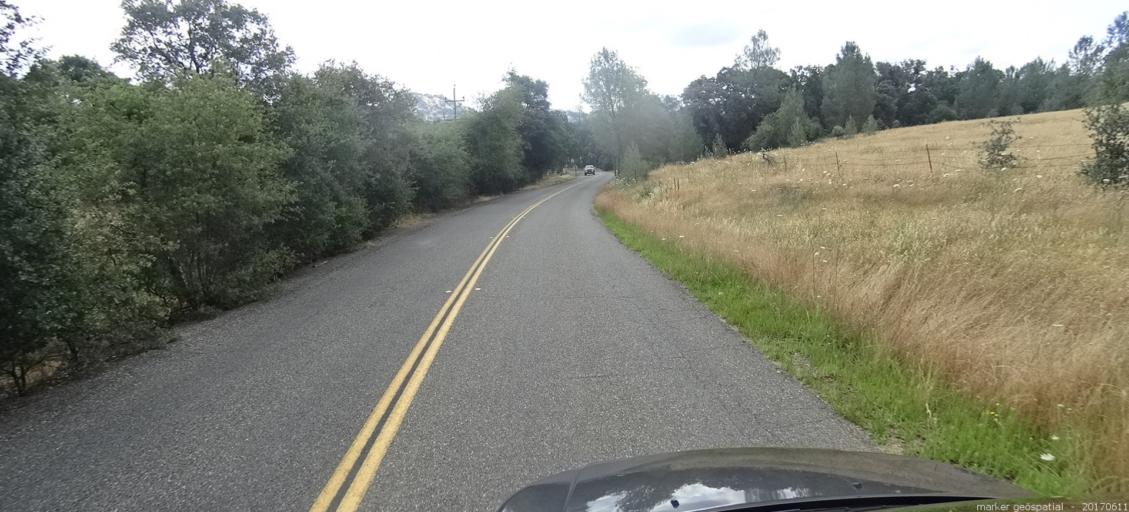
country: US
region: California
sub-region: Yuba County
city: Loma Rica
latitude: 39.3801
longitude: -121.3904
